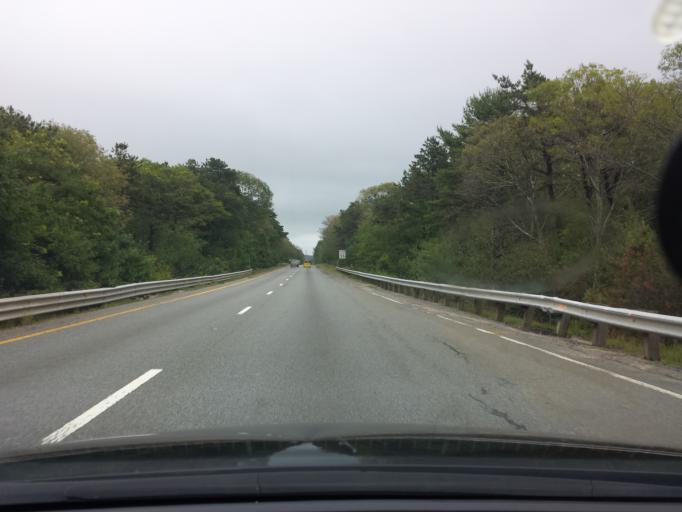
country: US
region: Massachusetts
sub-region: Barnstable County
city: West Barnstable
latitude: 41.7055
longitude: -70.4031
